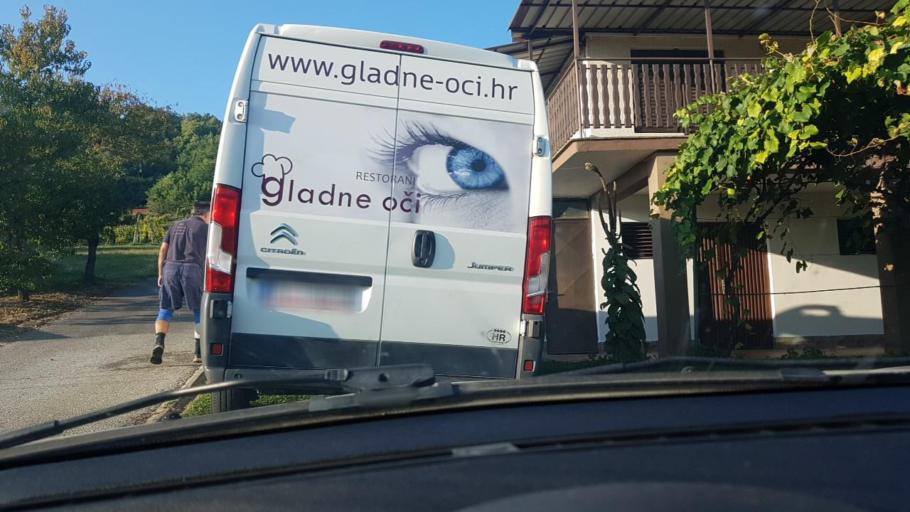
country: HR
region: Krapinsko-Zagorska
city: Radoboj
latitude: 46.1638
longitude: 15.9390
